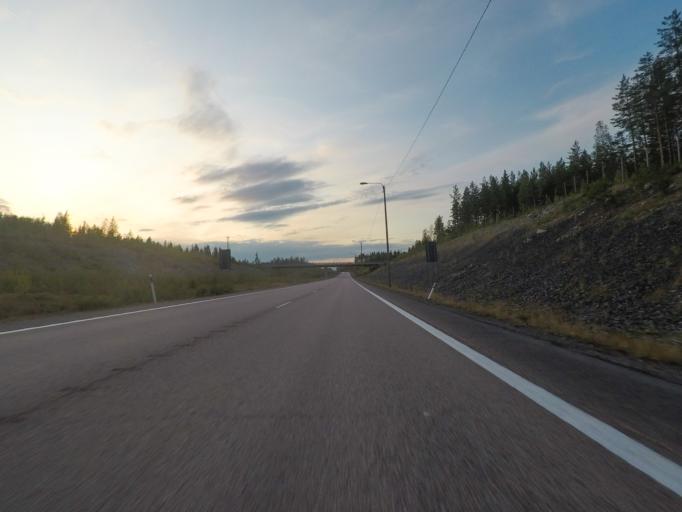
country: FI
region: Central Finland
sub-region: Jyvaeskylae
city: Toivakka
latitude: 62.1048
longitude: 25.9808
